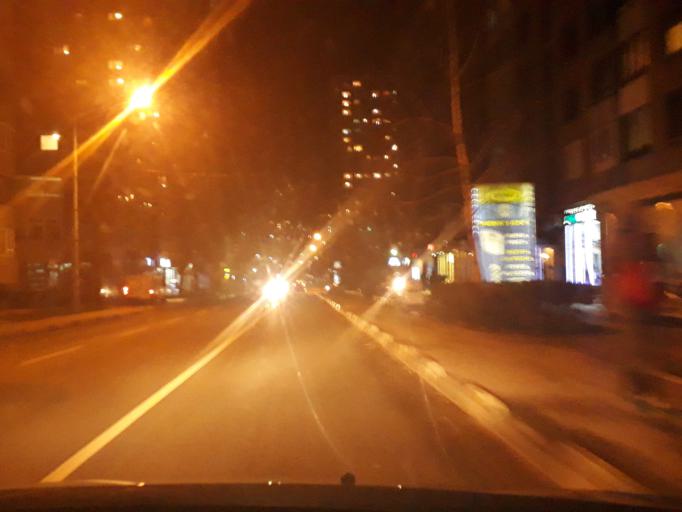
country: BA
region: Federation of Bosnia and Herzegovina
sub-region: Kanton Sarajevo
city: Sarajevo
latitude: 43.8472
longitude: 18.3745
